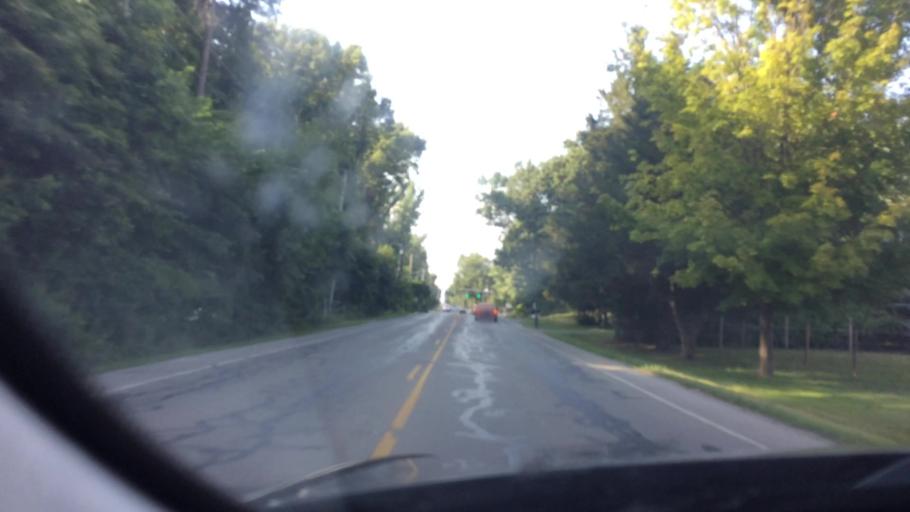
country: US
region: Ohio
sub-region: Lucas County
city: Holland
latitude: 41.6572
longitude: -83.7222
